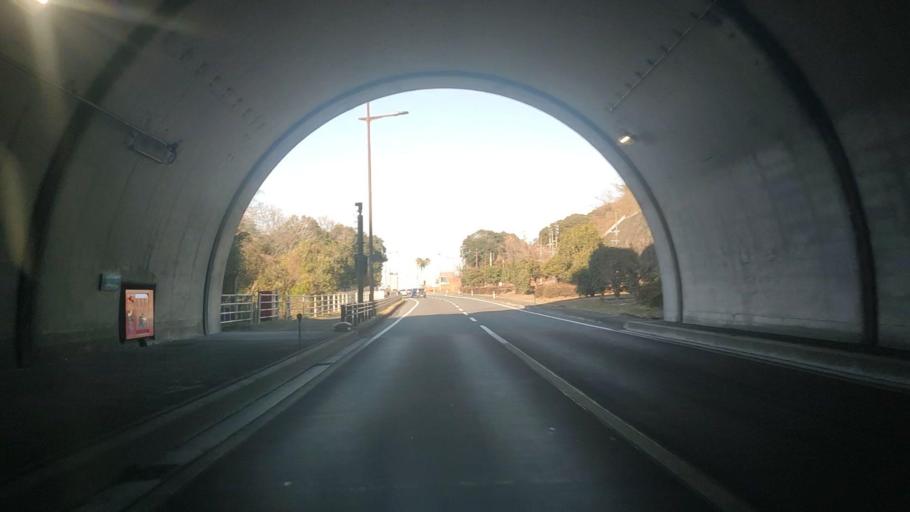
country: JP
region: Oita
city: Oita
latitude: 33.0953
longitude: 131.6507
